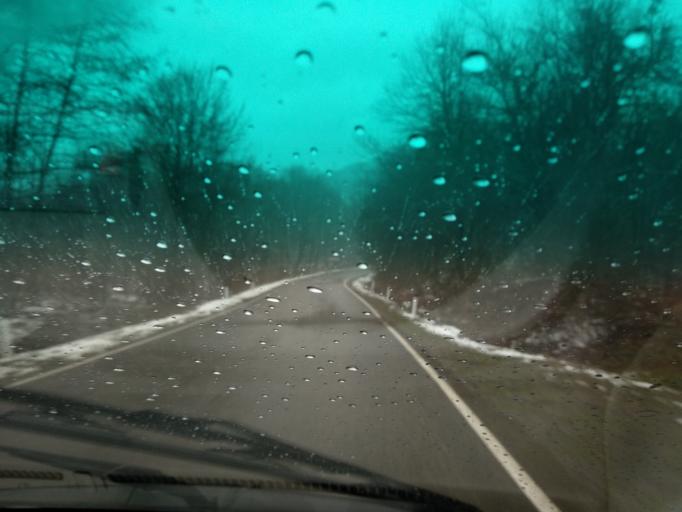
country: RU
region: Krasnodarskiy
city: Khadyzhensk
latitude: 44.2601
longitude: 39.3656
